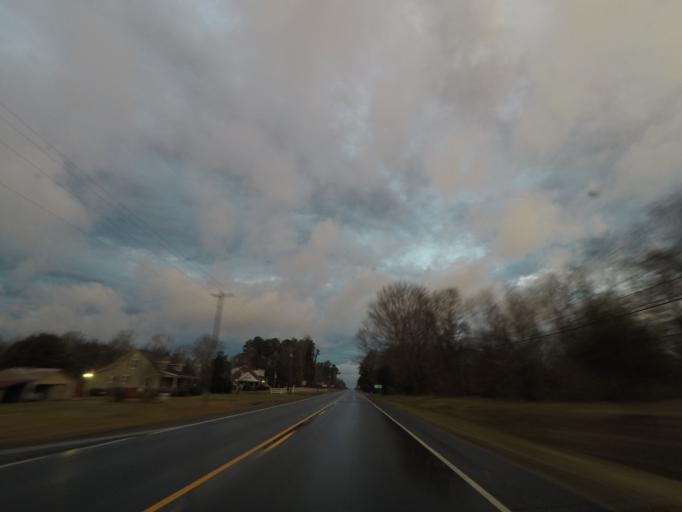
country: US
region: North Carolina
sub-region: Alamance County
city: Mebane
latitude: 36.2497
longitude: -79.1906
